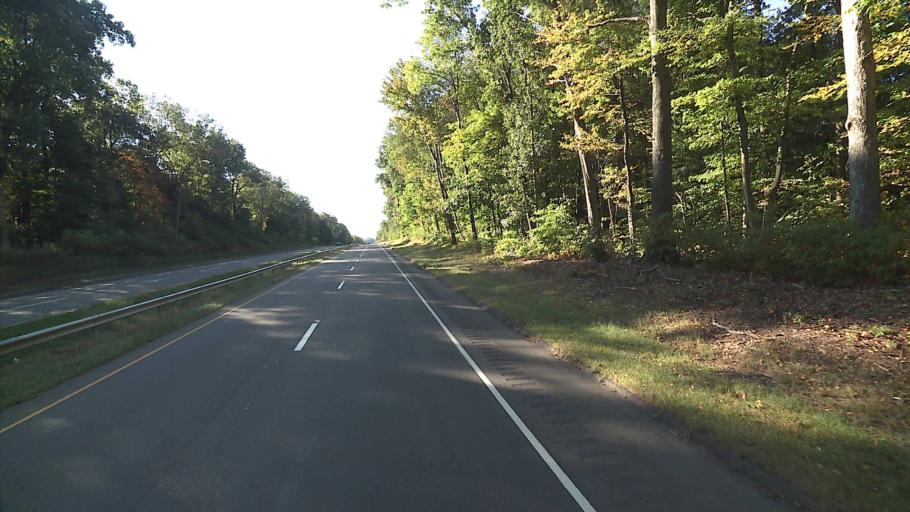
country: US
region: Connecticut
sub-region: New Haven County
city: Meriden
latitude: 41.5538
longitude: -72.7748
